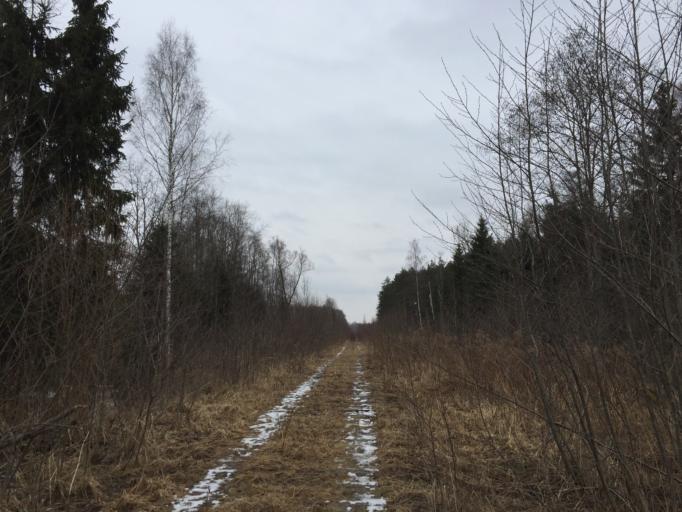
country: LV
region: Lielvarde
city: Lielvarde
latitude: 56.7602
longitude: 24.8182
